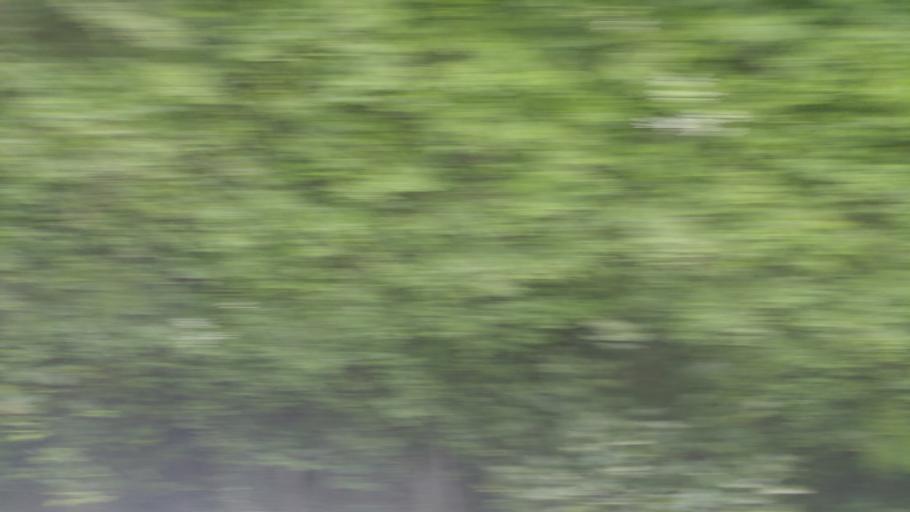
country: NO
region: Sor-Trondelag
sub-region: Melhus
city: Lundamo
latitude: 63.1557
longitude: 10.2841
